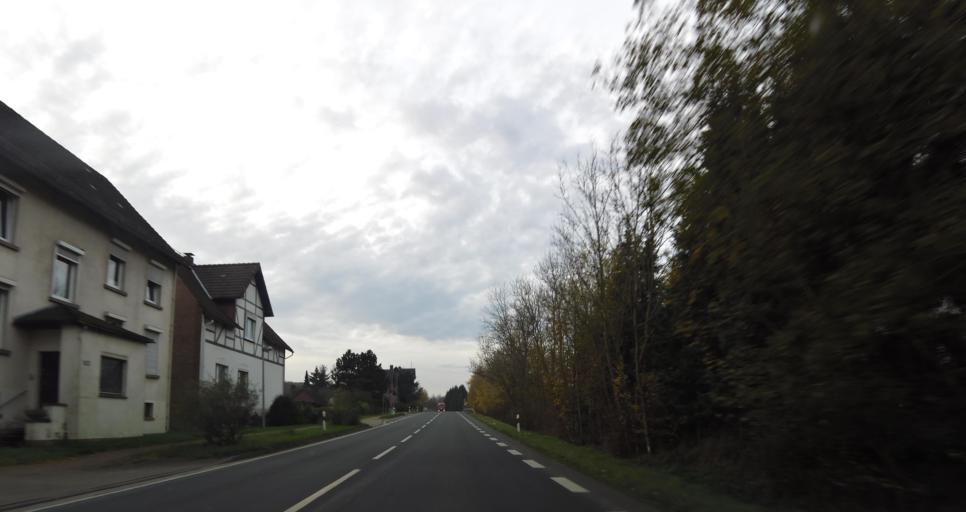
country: DE
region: Lower Saxony
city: Lenne
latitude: 51.8957
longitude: 9.7012
